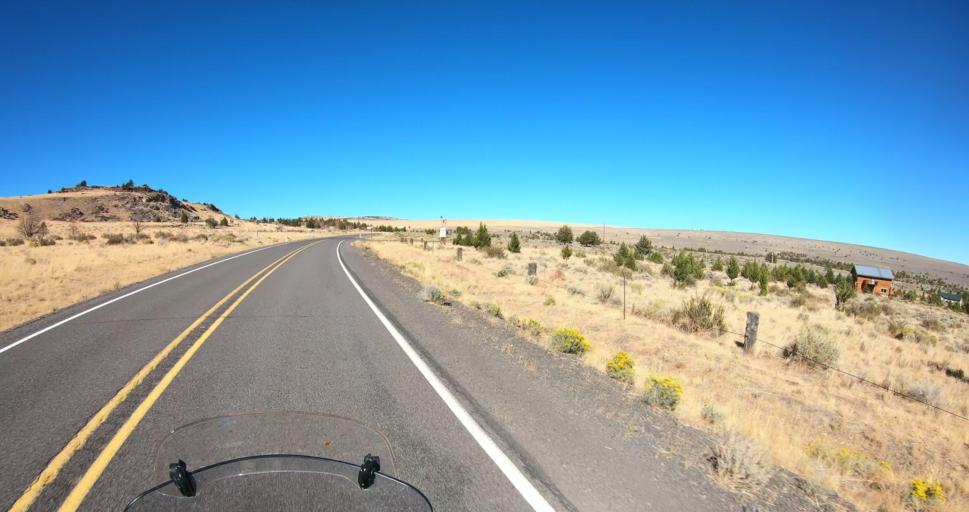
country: US
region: Oregon
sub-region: Lake County
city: Lakeview
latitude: 43.0046
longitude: -120.7761
